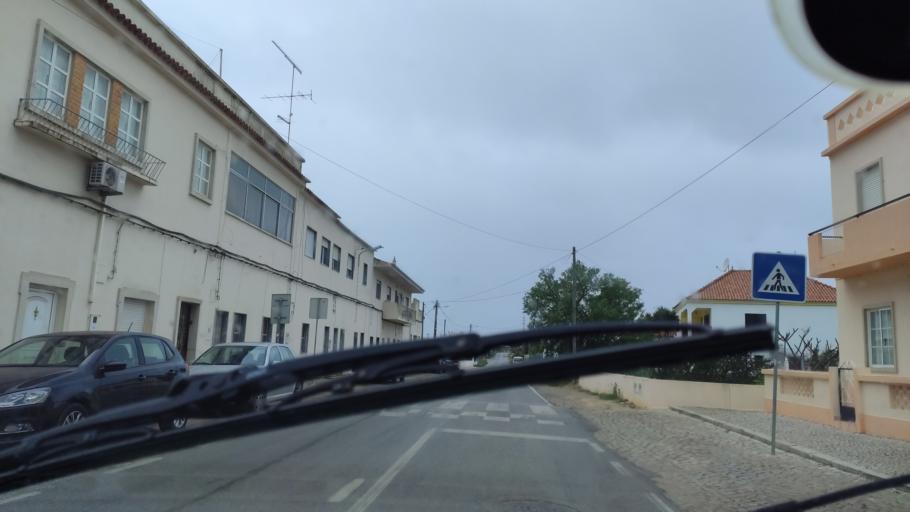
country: PT
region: Faro
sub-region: Faro
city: Santa Barbara de Nexe
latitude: 37.0744
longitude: -7.9361
